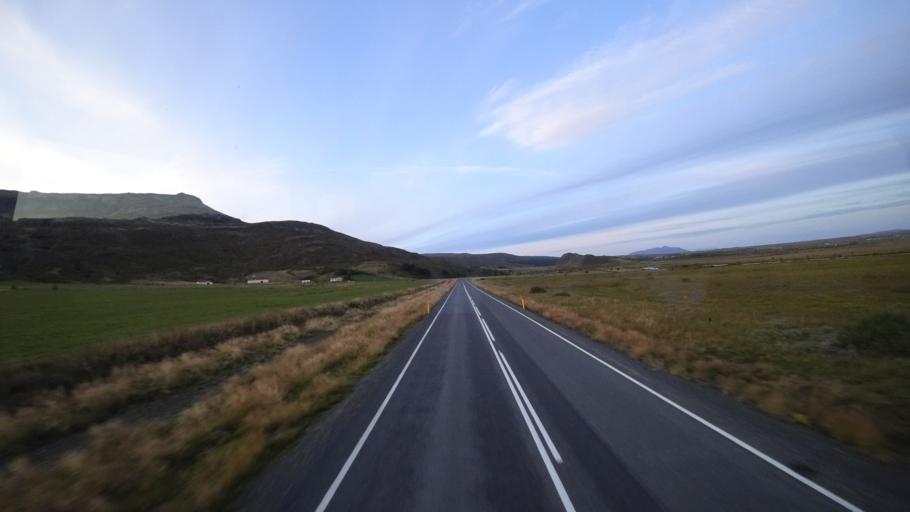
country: IS
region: South
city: Selfoss
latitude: 64.2975
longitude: -20.3330
